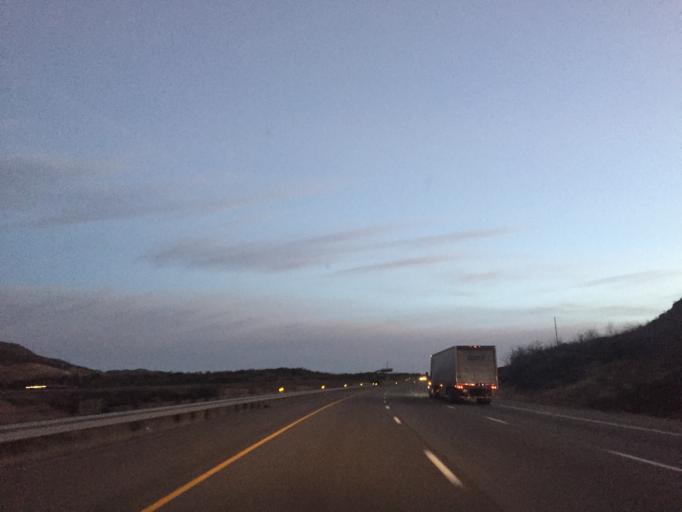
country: US
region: Utah
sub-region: Washington County
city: Toquerville
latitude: 37.3068
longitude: -113.2975
